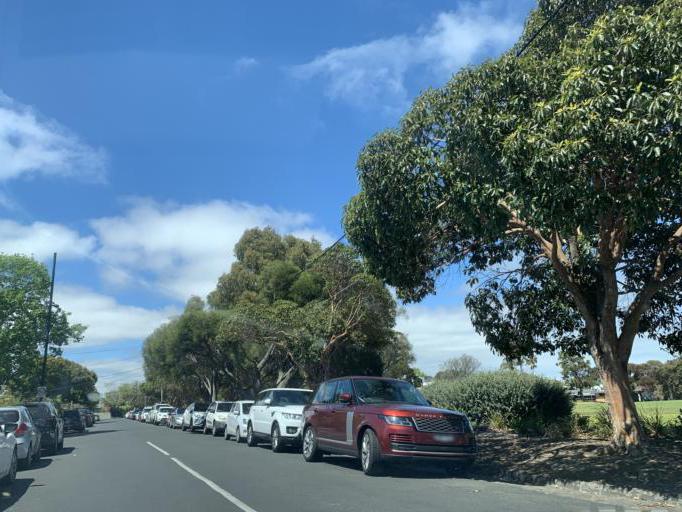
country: AU
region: Victoria
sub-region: Bayside
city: North Brighton
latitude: -37.9082
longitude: 144.9938
